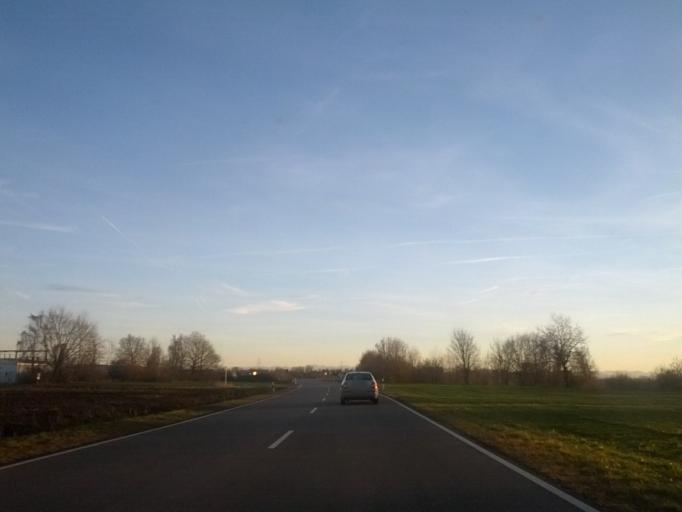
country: DE
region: Bavaria
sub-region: Swabia
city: Heimertingen
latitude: 48.0529
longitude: 10.1531
